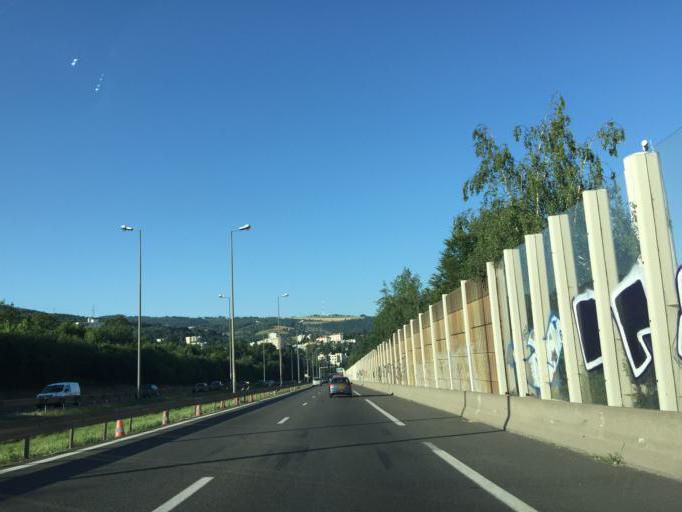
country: FR
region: Rhone-Alpes
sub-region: Departement de la Loire
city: Saint-Etienne
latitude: 45.4266
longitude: 4.4152
